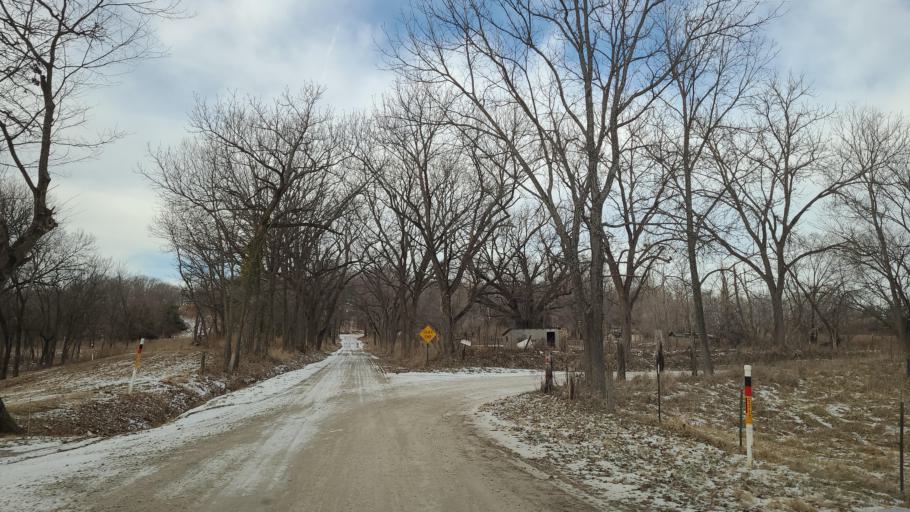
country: US
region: Kansas
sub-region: Jefferson County
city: Oskaloosa
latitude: 39.0583
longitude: -95.4233
